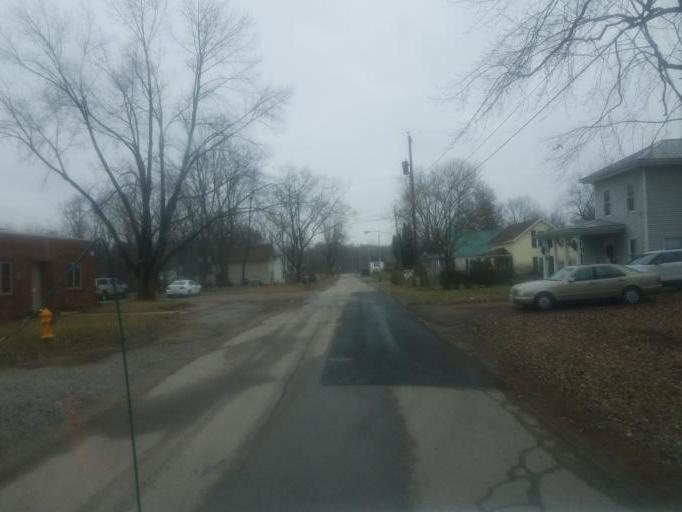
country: US
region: Ohio
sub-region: Delaware County
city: Sunbury
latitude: 40.2211
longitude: -82.8798
